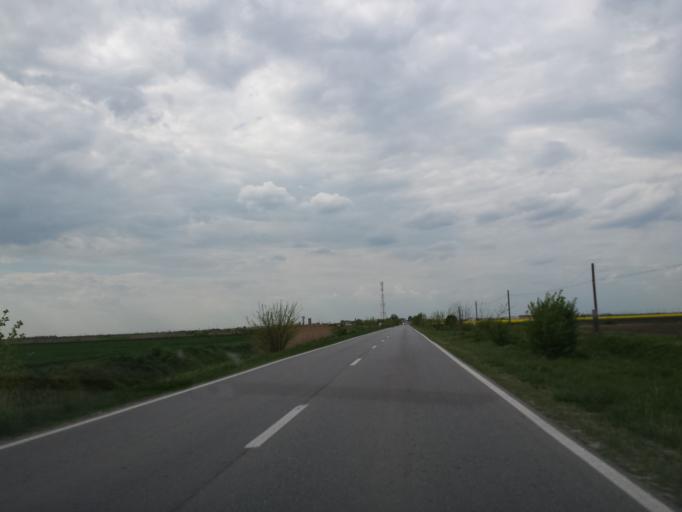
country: RO
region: Timis
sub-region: Comuna Sanpetru Mare
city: Sanpetru Mare
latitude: 46.0409
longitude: 20.6536
